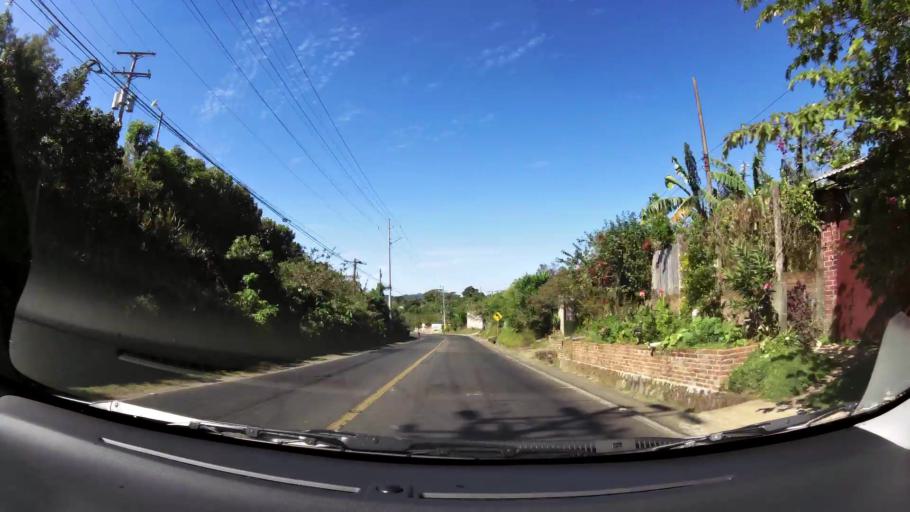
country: SV
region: Ahuachapan
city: Concepcion de Ataco
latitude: 13.8496
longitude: -89.8221
